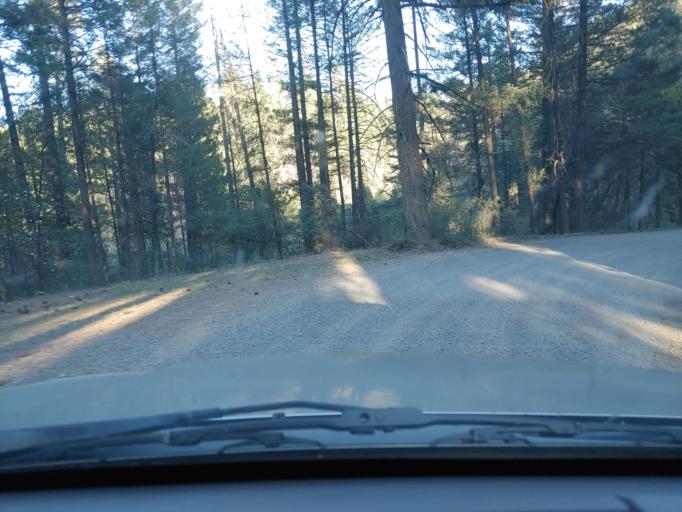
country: US
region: California
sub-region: Shasta County
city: Bella Vista
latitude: 40.8258
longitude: -122.0176
